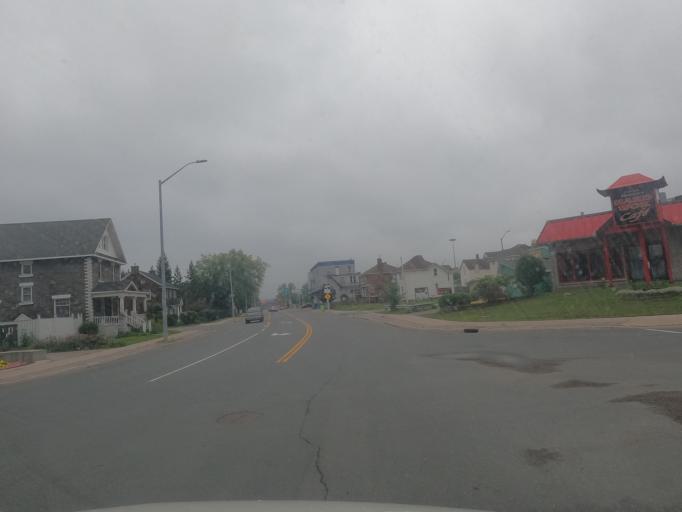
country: CA
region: Ontario
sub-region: Algoma
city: Sault Ste. Marie
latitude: 46.5209
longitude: -84.3473
